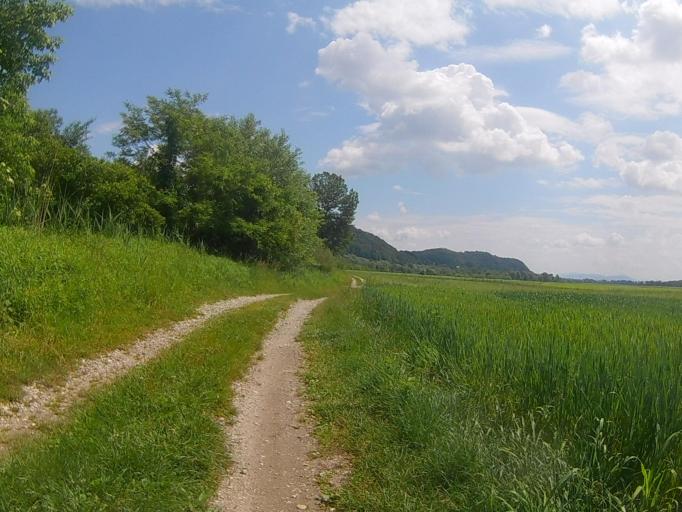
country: SI
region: Starse
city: Starse
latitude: 46.4566
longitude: 15.8130
